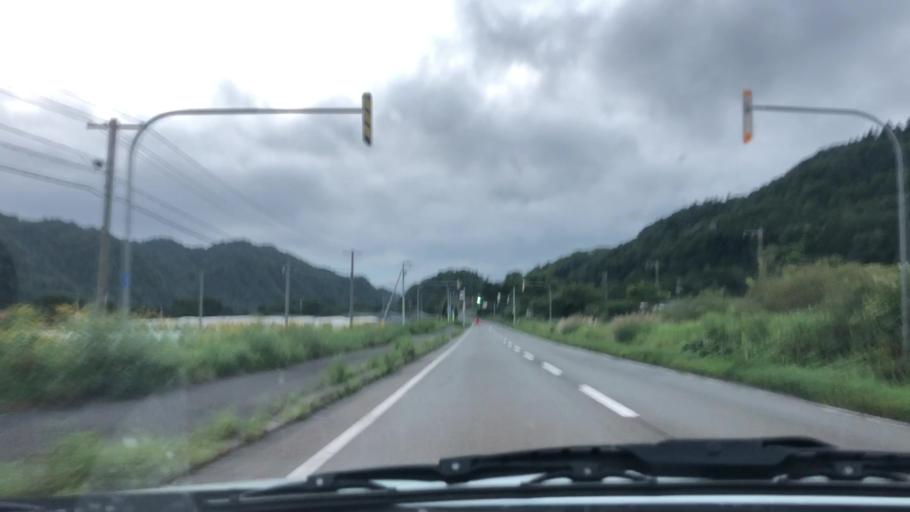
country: JP
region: Hokkaido
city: Chitose
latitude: 42.9057
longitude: 141.9948
